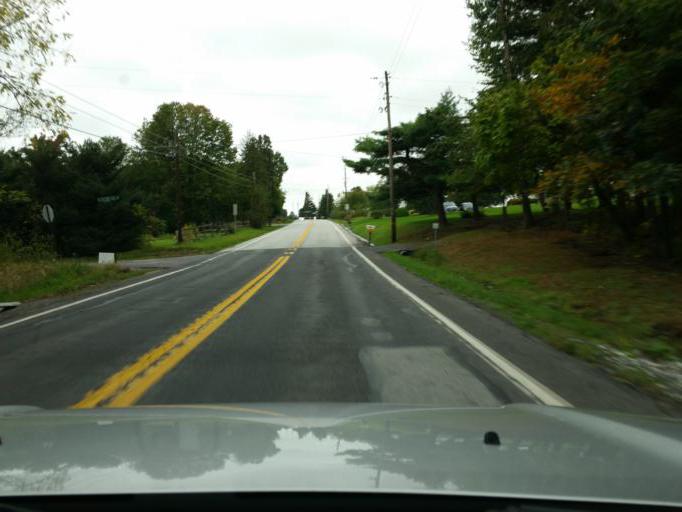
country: US
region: Pennsylvania
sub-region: Adams County
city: Biglerville
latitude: 39.9439
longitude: -77.1887
